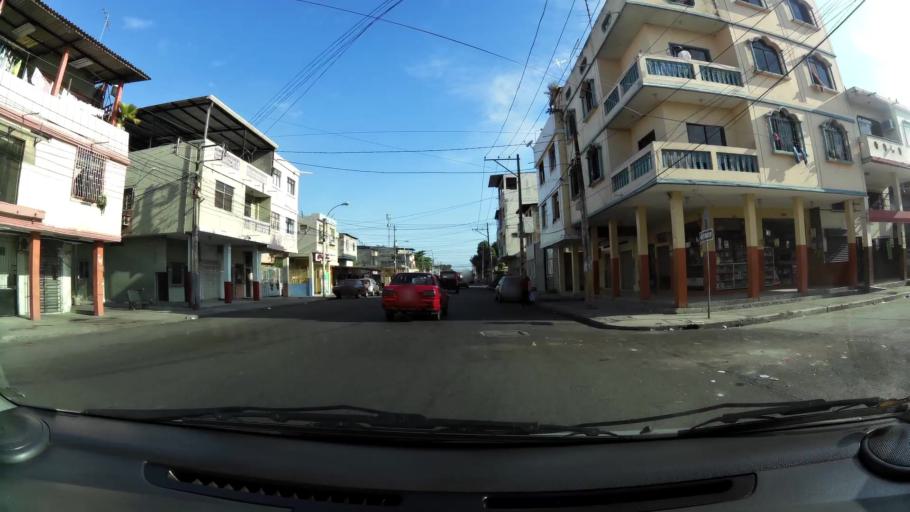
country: EC
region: Guayas
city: Guayaquil
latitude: -2.2156
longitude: -79.9026
